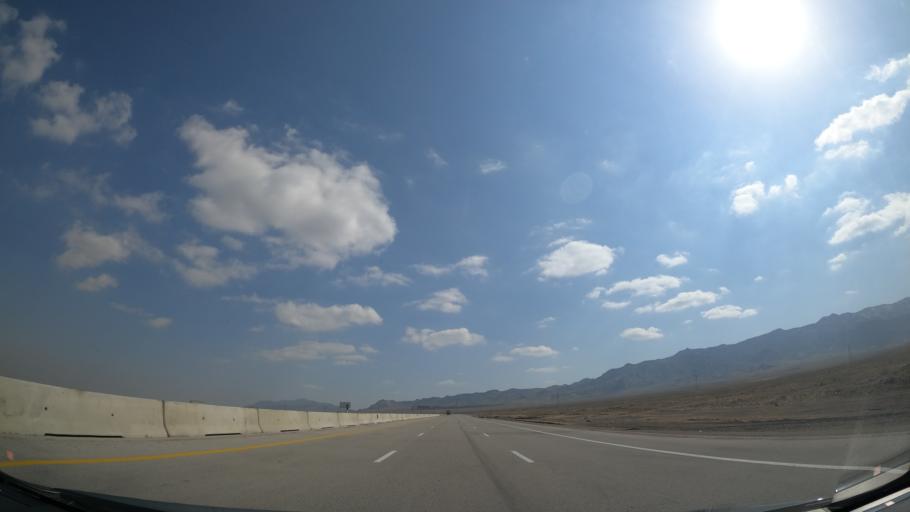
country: IR
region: Alborz
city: Eshtehard
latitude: 35.7212
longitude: 50.5693
